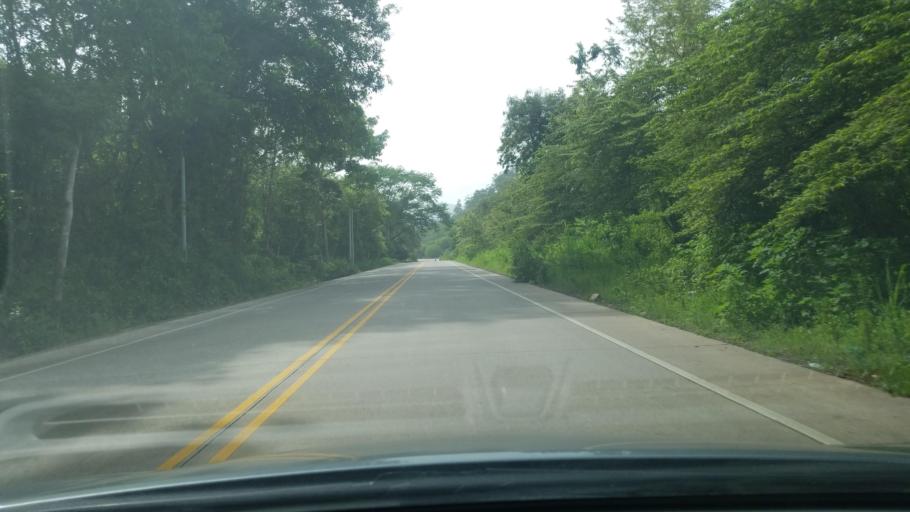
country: HN
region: Copan
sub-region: Santa Rita
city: Santa Rita, Copan
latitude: 14.8707
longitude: -89.0763
